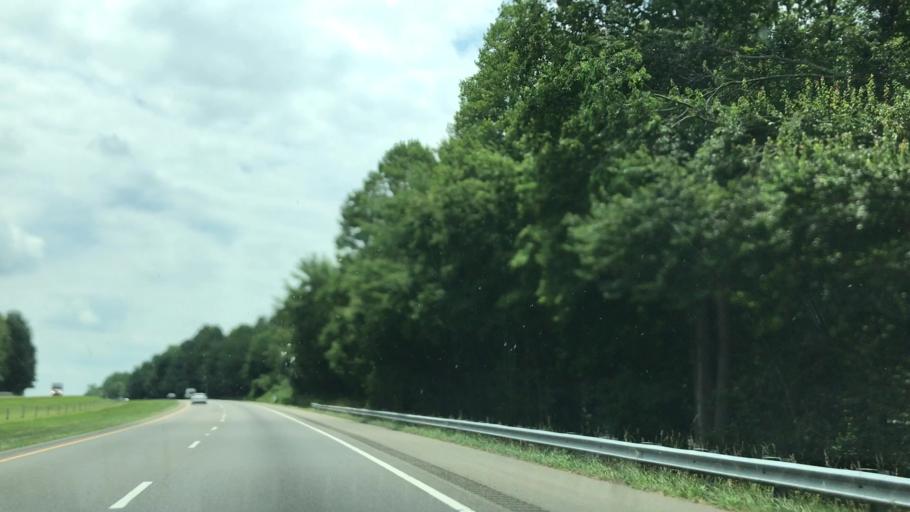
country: US
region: North Carolina
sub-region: Surry County
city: Dobson
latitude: 36.4597
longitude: -80.7676
